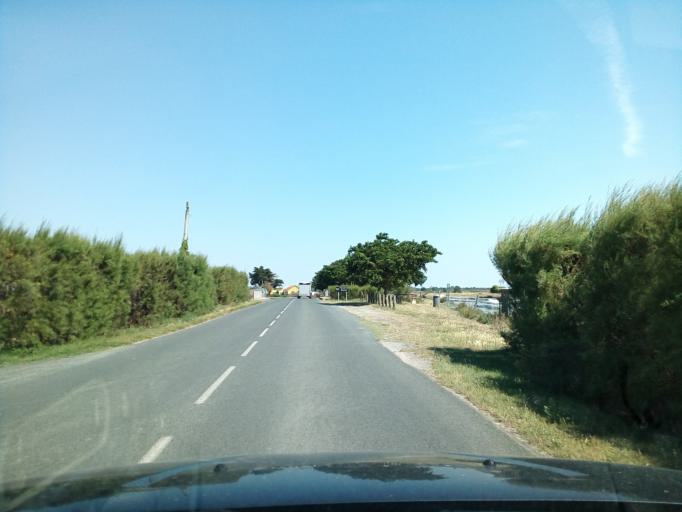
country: FR
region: Poitou-Charentes
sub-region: Departement de la Charente-Maritime
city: Boyard-Ville
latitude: 45.9667
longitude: -1.2619
